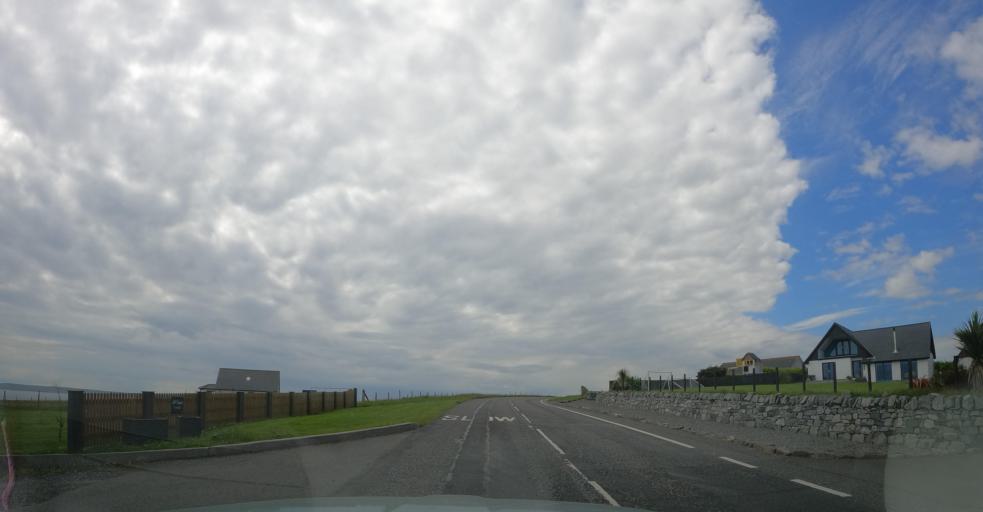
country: GB
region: Scotland
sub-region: Eilean Siar
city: Isle of Lewis
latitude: 58.2813
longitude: -6.2836
